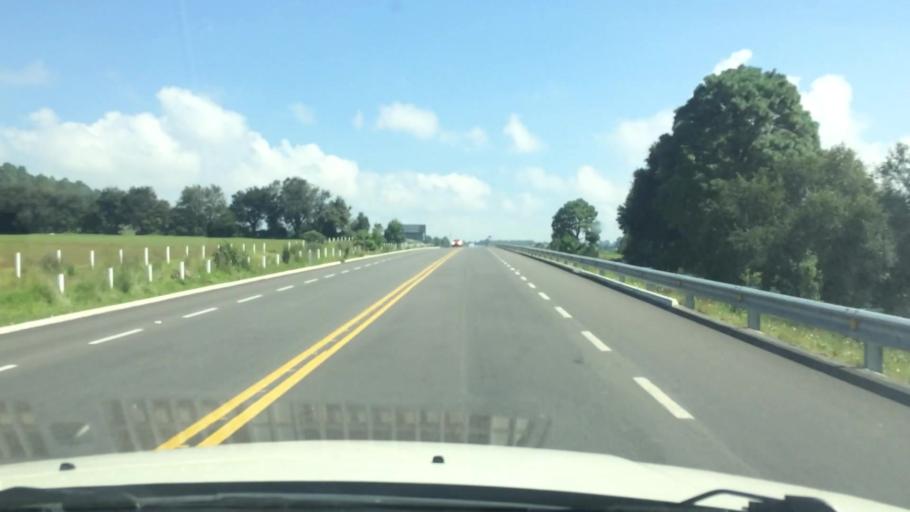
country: MX
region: Mexico
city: Amanalco de Becerra
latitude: 19.3119
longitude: -100.0057
